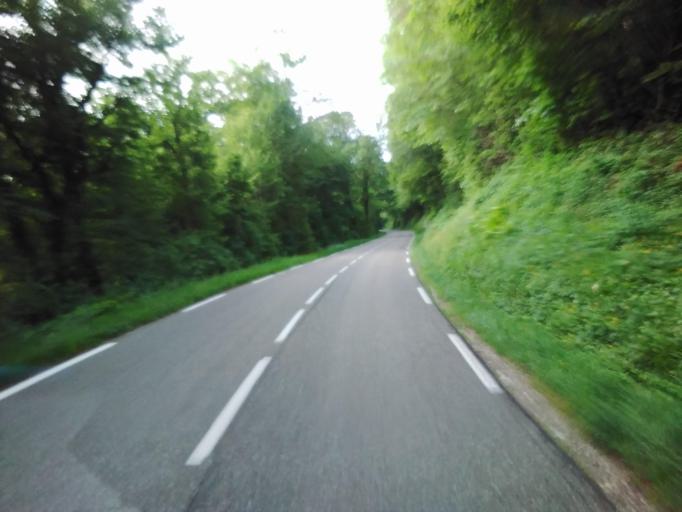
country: FR
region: Franche-Comte
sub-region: Departement du Jura
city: Arbois
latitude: 46.8947
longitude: 5.7953
